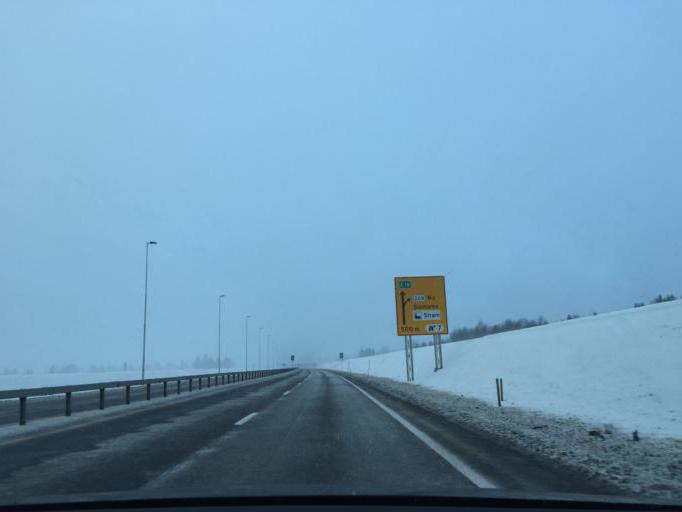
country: NO
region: Hedmark
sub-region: Sor-Odal
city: Skarnes
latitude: 60.2461
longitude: 11.7604
